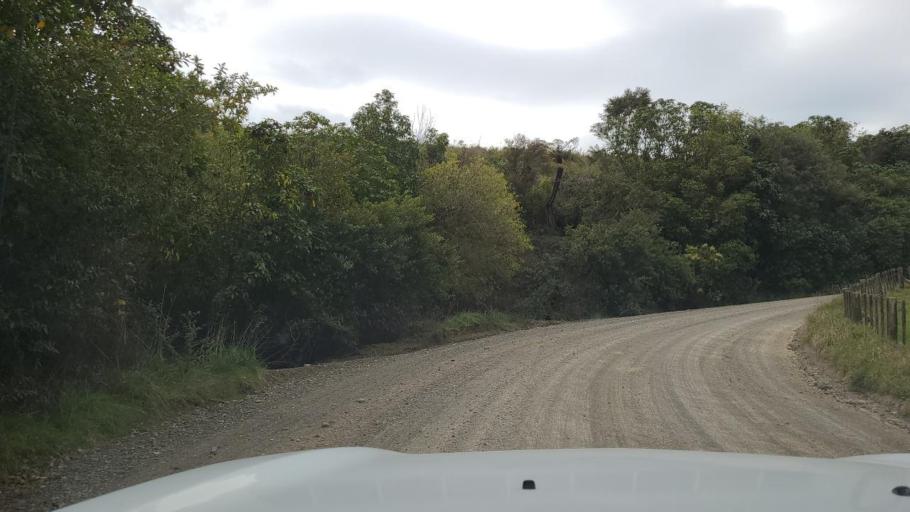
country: NZ
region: Hawke's Bay
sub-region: Napier City
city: Napier
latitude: -39.1863
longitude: 176.9436
